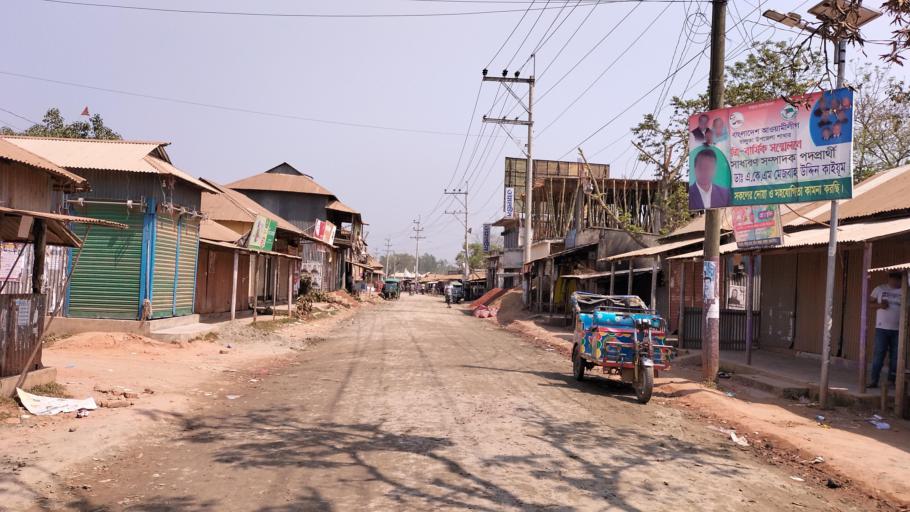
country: BD
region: Dhaka
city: Sakhipur
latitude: 24.3078
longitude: 90.3179
